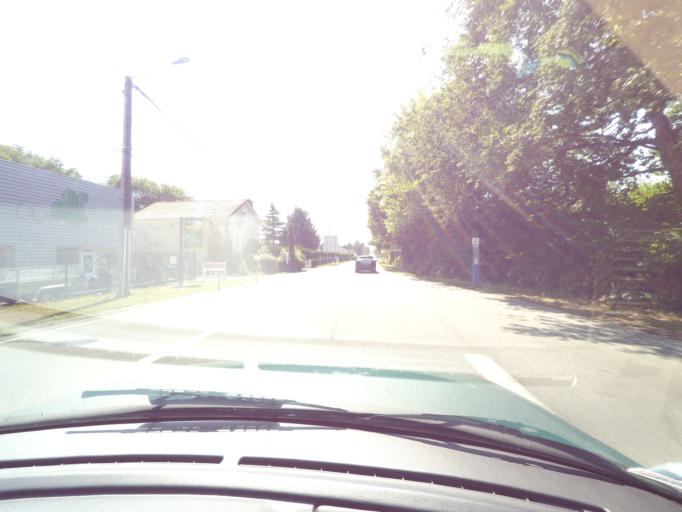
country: FR
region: Limousin
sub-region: Departement de la Haute-Vienne
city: Couzeix
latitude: 45.8997
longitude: 1.2270
